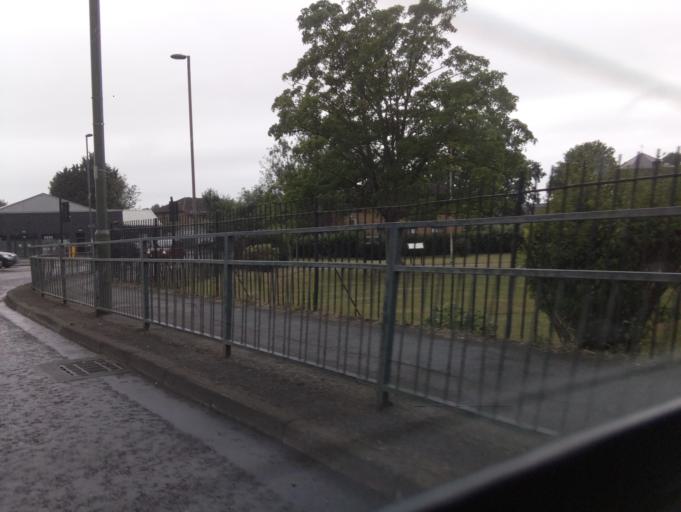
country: GB
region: England
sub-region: Surrey
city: Horley
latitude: 51.1748
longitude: -0.1699
